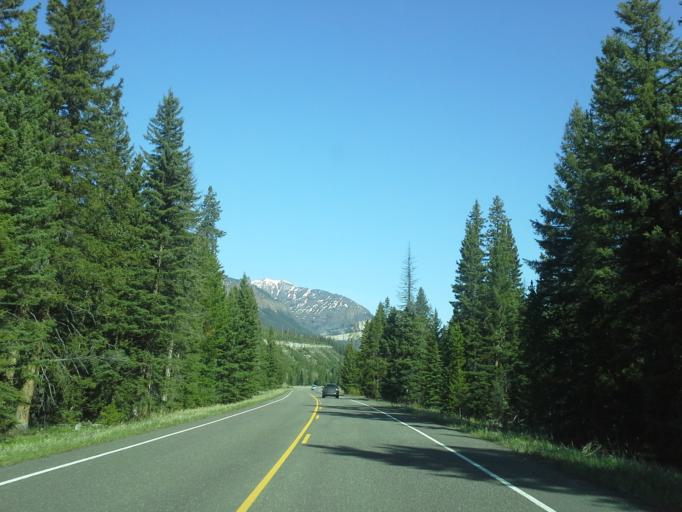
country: US
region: Montana
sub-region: Carbon County
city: Red Lodge
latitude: 44.9605
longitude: -109.8178
